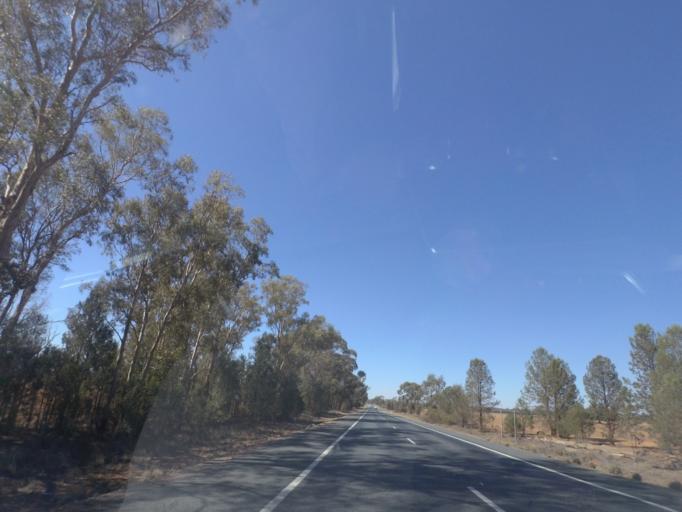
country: AU
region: New South Wales
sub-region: Bland
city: West Wyalong
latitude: -34.1854
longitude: 147.1126
